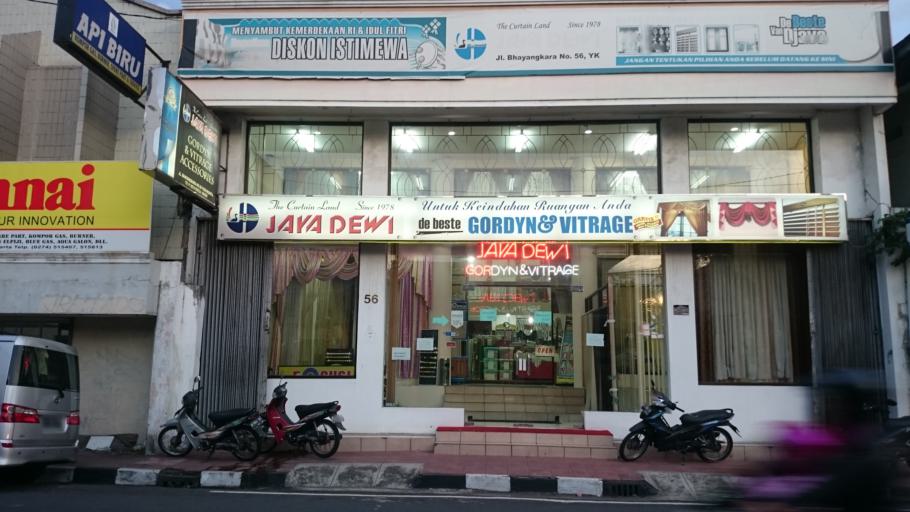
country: ID
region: Daerah Istimewa Yogyakarta
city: Yogyakarta
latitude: -7.7976
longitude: 110.3622
